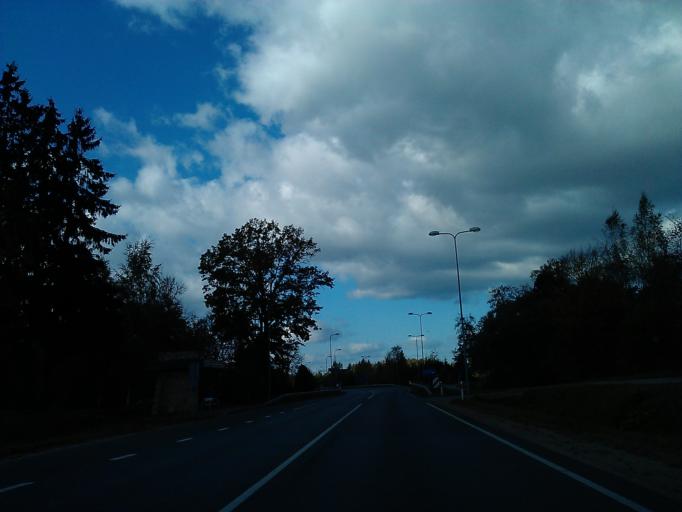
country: LV
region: Livani
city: Livani
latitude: 56.3880
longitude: 26.1533
